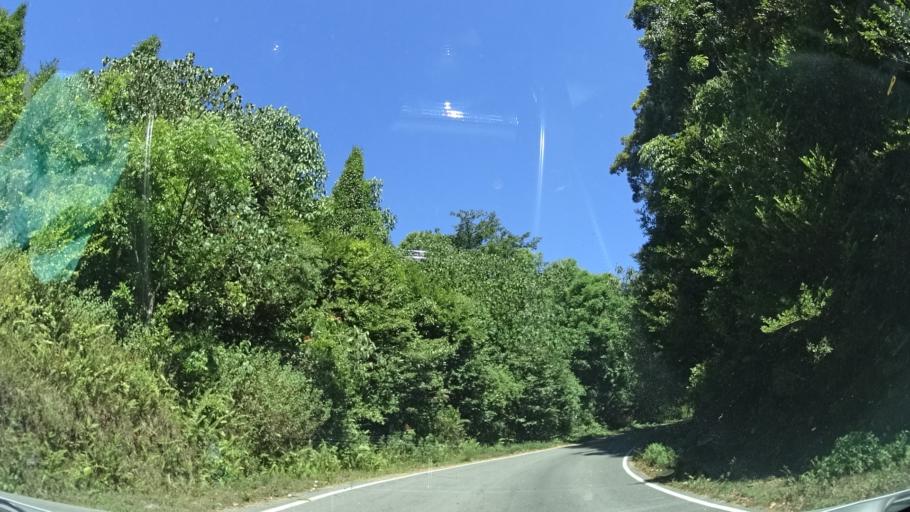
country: IN
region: Karnataka
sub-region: Udupi
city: Karkal
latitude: 13.2379
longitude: 75.1752
